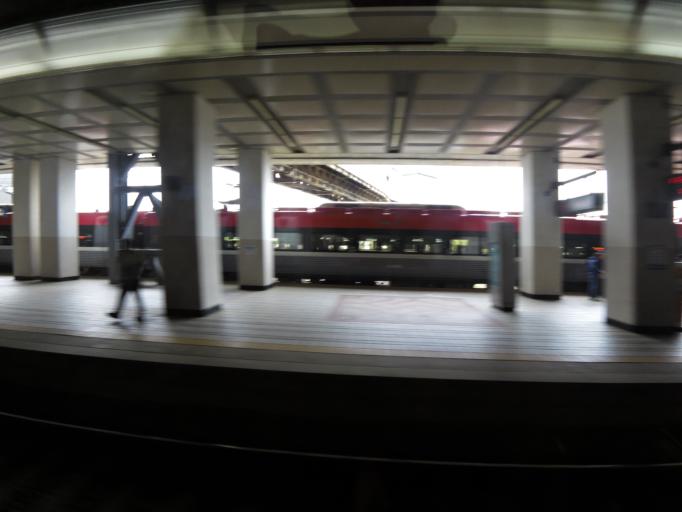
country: KR
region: Seoul
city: Seoul
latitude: 37.5302
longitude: 126.9640
